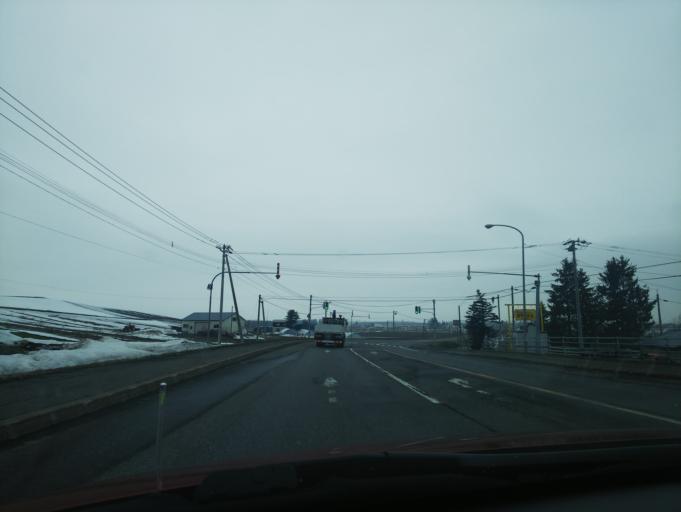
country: JP
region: Hokkaido
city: Nayoro
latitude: 44.0634
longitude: 142.4006
